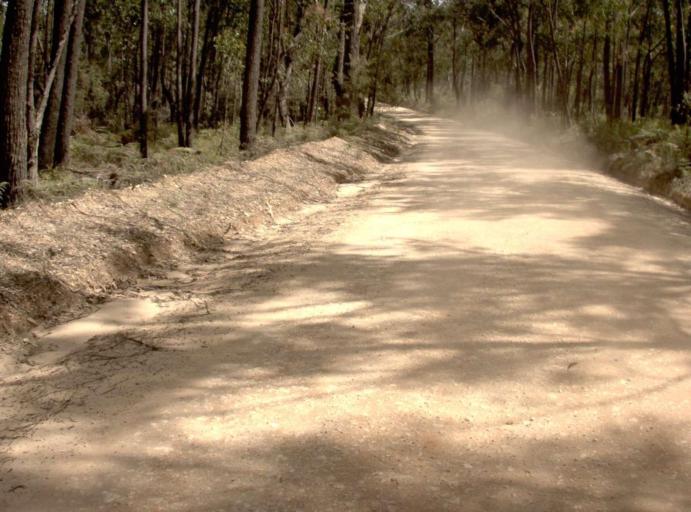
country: AU
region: Victoria
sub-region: East Gippsland
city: Lakes Entrance
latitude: -37.6619
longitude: 148.6350
